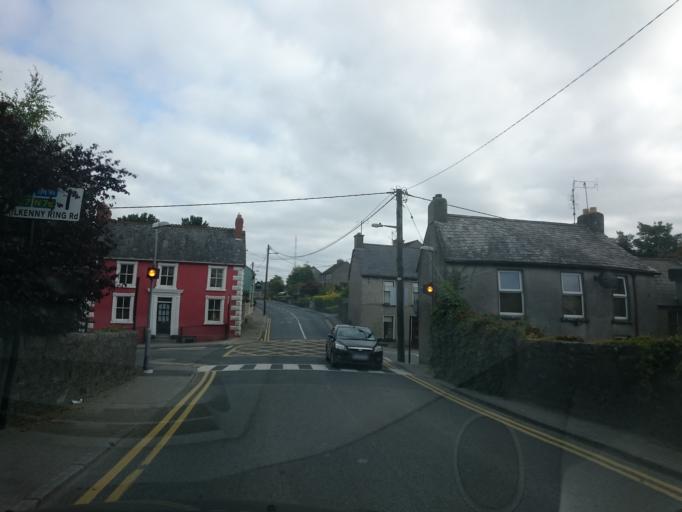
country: IE
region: Leinster
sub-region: Kilkenny
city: Kilkenny
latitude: 52.6582
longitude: -7.2533
